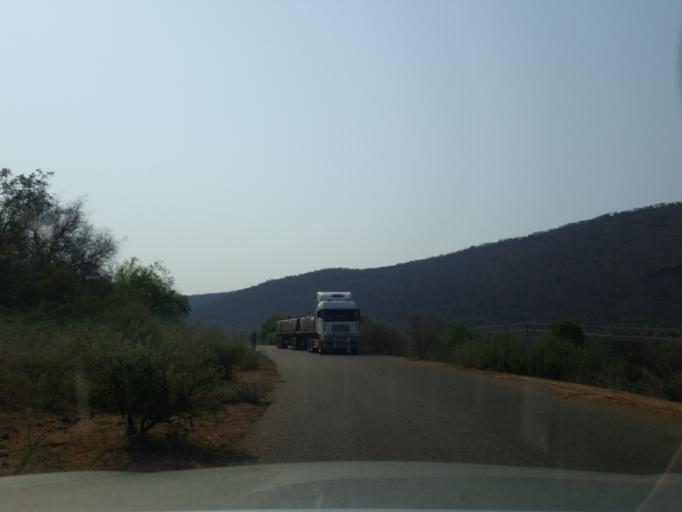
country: BW
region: South East
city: Lobatse
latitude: -25.3291
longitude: 25.7781
